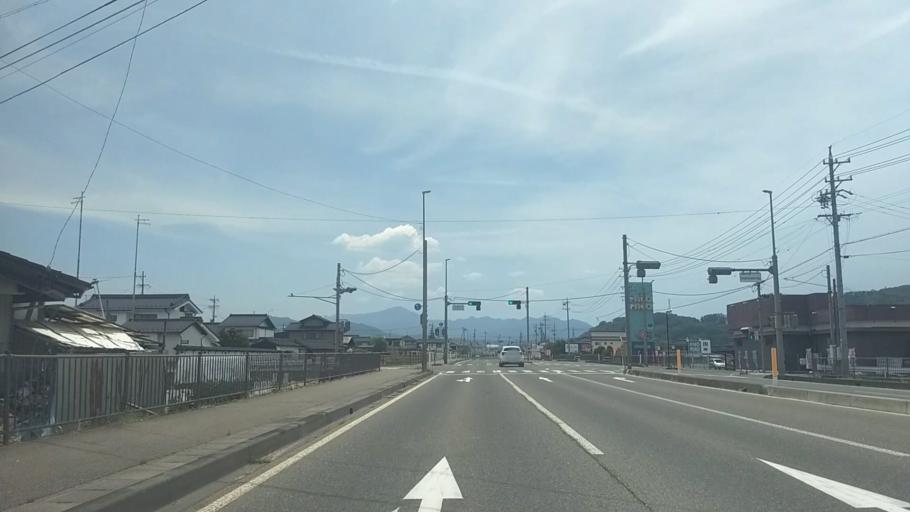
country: JP
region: Nagano
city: Saku
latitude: 36.2143
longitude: 138.4636
